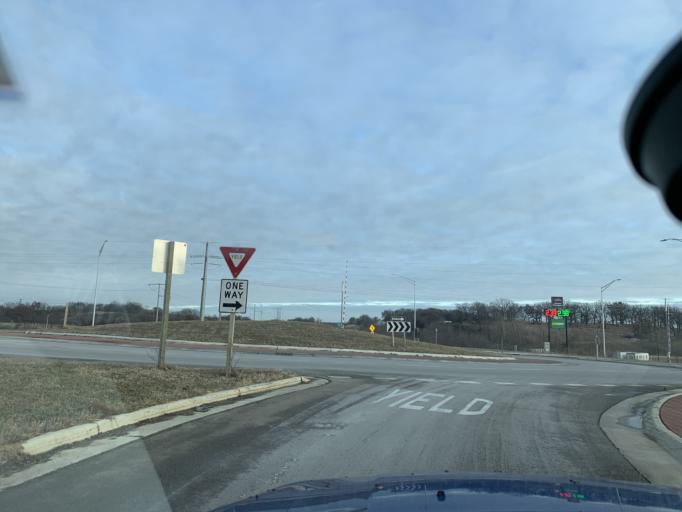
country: US
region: Wisconsin
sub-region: Dane County
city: Cottage Grove
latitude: 43.0007
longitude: -89.2013
